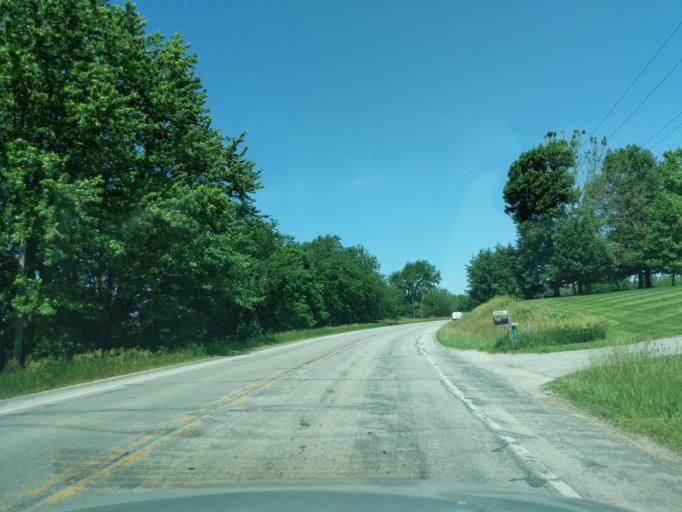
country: US
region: Indiana
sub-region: Whitley County
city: Columbia City
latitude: 41.1202
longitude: -85.4788
